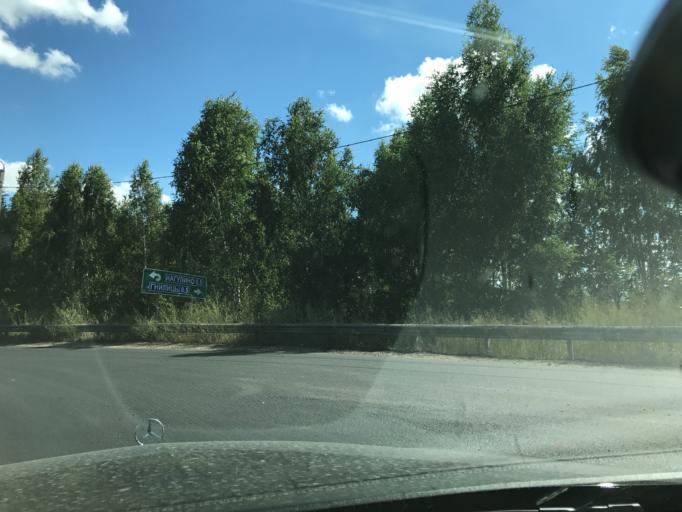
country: RU
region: Nizjnij Novgorod
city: Gorbatovka
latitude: 56.2183
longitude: 43.7550
